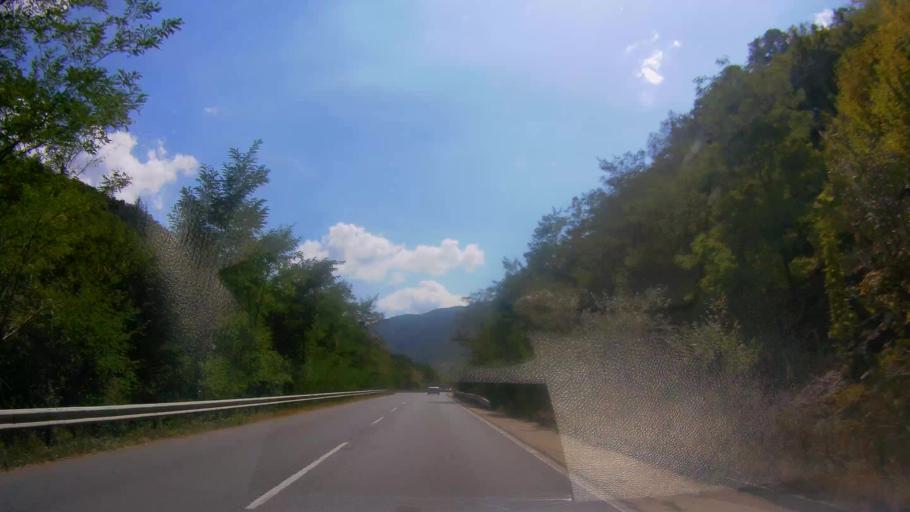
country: BG
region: Stara Zagora
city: Gurkovo
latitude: 42.7234
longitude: 25.7135
